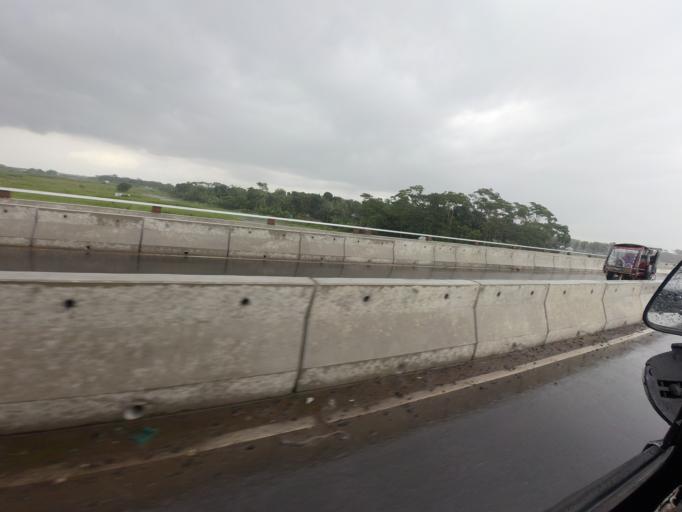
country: BD
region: Dhaka
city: Char Bhadrasan
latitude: 23.3998
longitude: 90.2006
